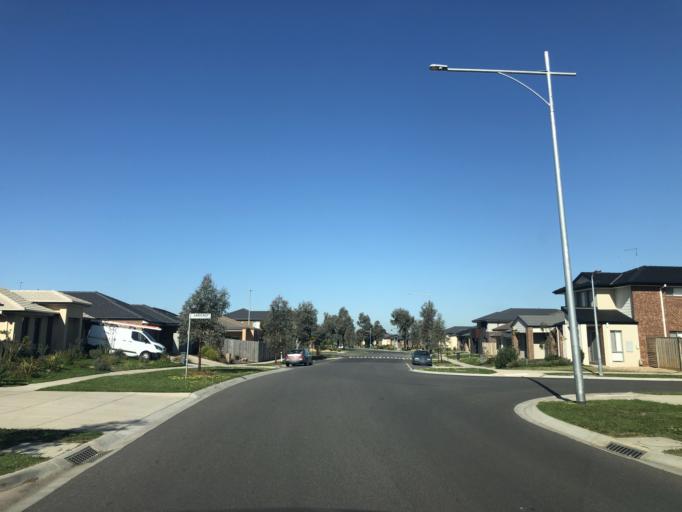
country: AU
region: Victoria
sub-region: Wyndham
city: Point Cook
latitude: -37.9044
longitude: 144.7227
